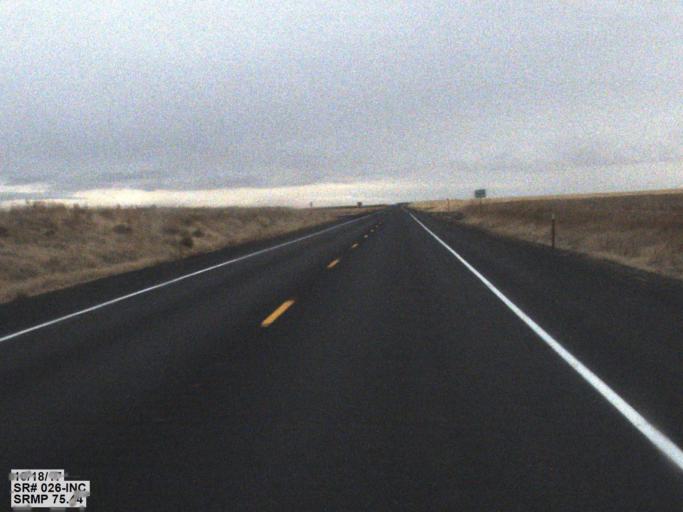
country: US
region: Washington
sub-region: Adams County
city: Ritzville
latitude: 46.7953
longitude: -118.4452
